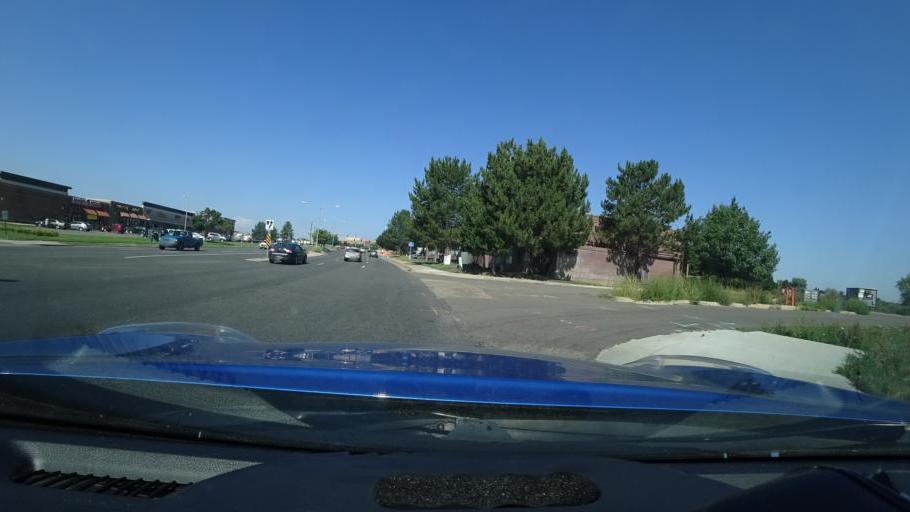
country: US
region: Colorado
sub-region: Adams County
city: Aurora
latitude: 39.7088
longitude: -104.8076
